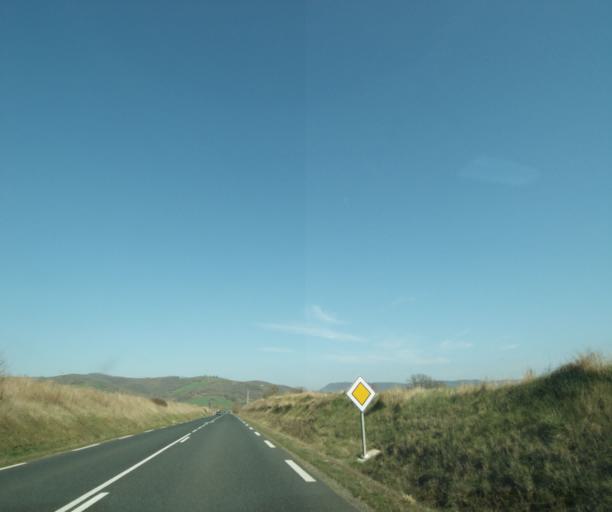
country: FR
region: Midi-Pyrenees
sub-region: Departement de l'Aveyron
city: Saint-Affrique
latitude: 43.9161
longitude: 2.8251
